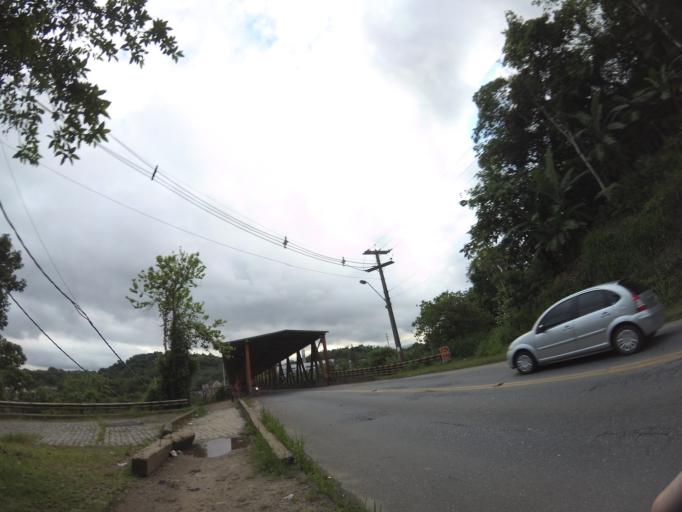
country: BR
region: Santa Catarina
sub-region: Blumenau
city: Blumenau
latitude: -26.8799
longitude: -49.1012
